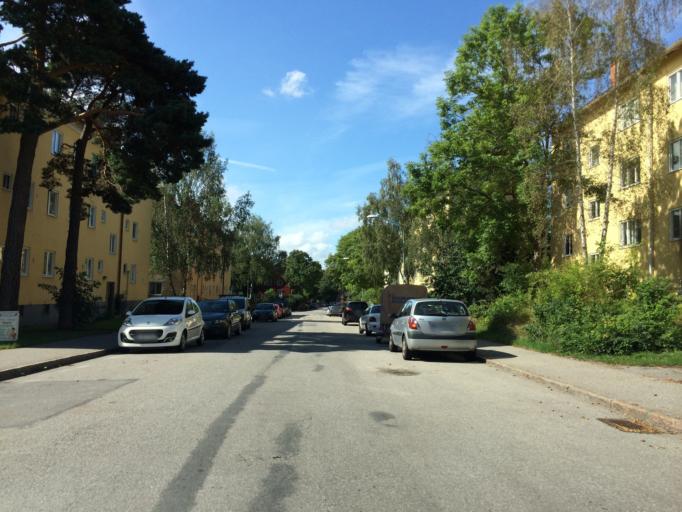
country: SE
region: Stockholm
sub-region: Huddinge Kommun
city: Huddinge
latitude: 59.2912
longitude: 17.9932
